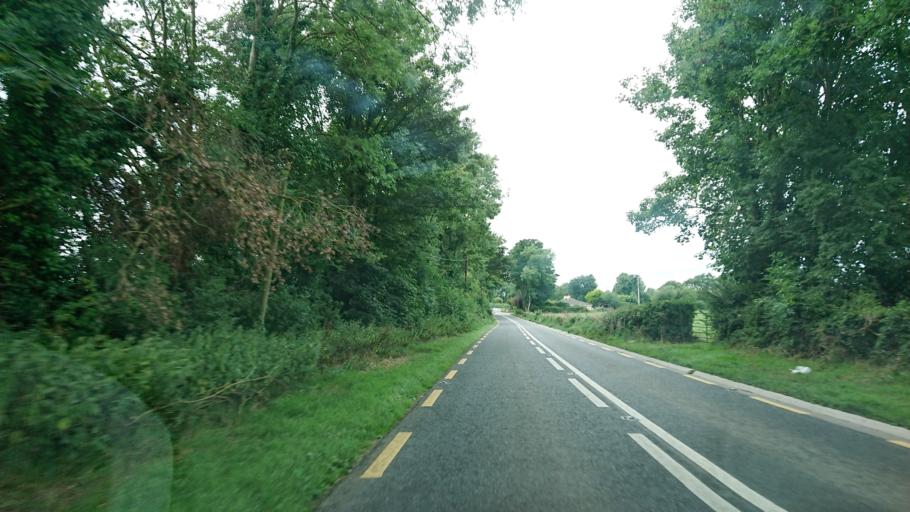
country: IE
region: Munster
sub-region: County Cork
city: Mallow
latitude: 52.1542
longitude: -8.5718
